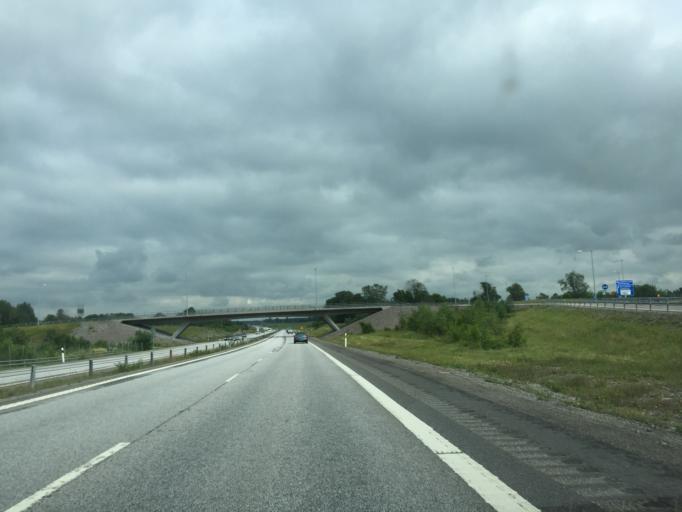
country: SE
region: OErebro
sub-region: Orebro Kommun
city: Vintrosa
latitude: 59.2462
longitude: 14.9435
